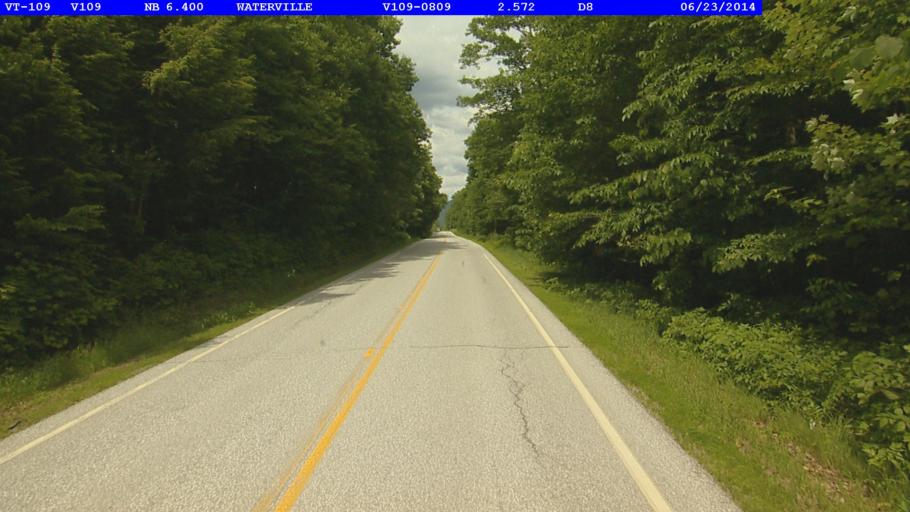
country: US
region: Vermont
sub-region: Lamoille County
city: Johnson
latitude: 44.7153
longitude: -72.7537
